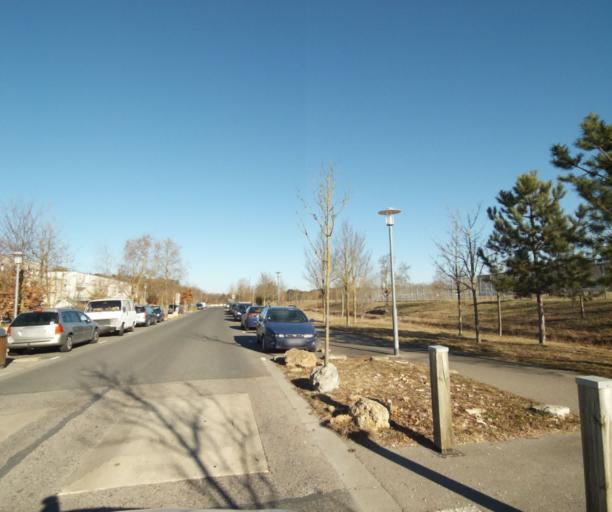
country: FR
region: Lorraine
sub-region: Departement de Meurthe-et-Moselle
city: Maxeville
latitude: 48.7068
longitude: 6.1486
